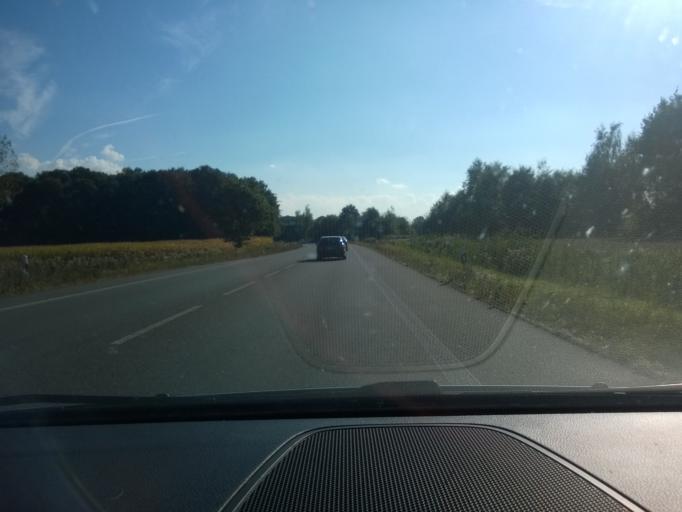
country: DE
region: North Rhine-Westphalia
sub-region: Regierungsbezirk Munster
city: Sudlohn
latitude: 51.8955
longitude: 6.8573
